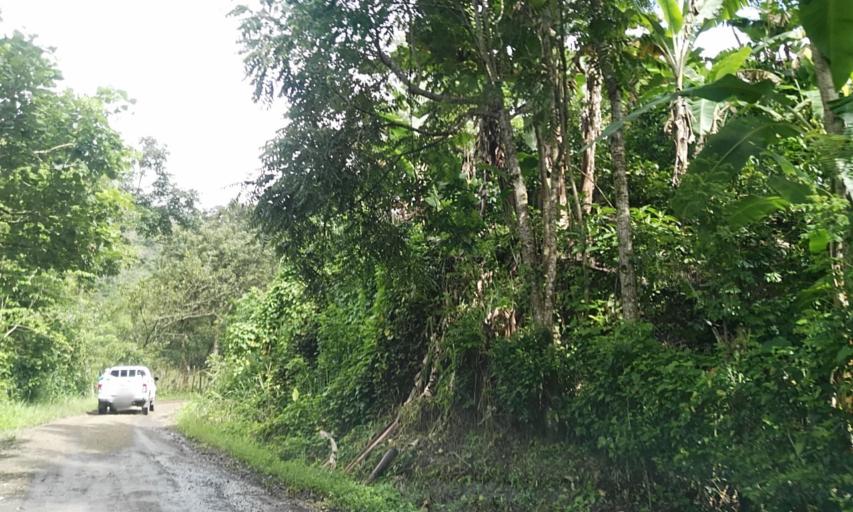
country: NI
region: Matagalpa
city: San Ramon
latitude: 12.9834
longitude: -85.8455
